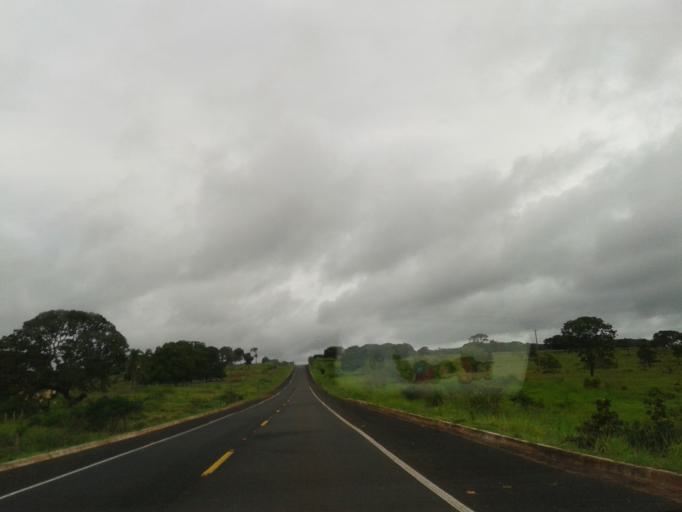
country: BR
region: Minas Gerais
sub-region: Santa Vitoria
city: Santa Vitoria
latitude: -19.2396
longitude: -50.0152
